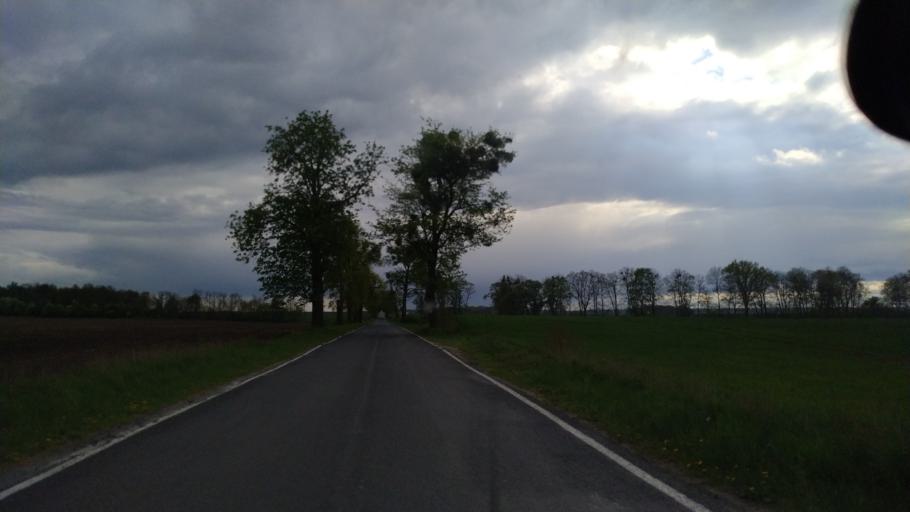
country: PL
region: Pomeranian Voivodeship
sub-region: Powiat starogardzki
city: Smetowo Graniczne
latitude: 53.7308
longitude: 18.6409
